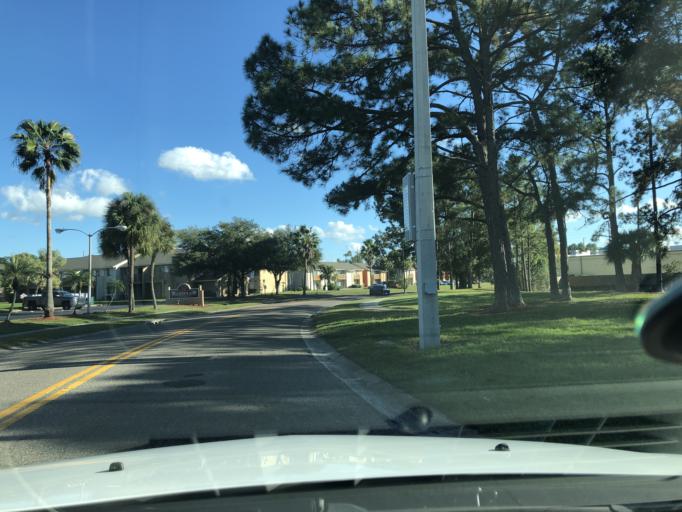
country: US
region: Florida
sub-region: Orange County
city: Oak Ridge
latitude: 28.4748
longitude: -81.4270
